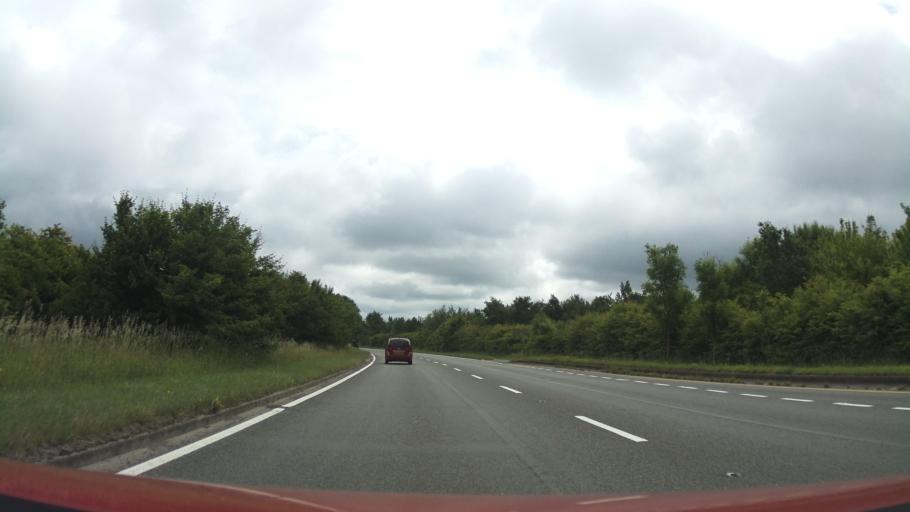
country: GB
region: England
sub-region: Leicestershire
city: Ashby de la Zouch
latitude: 52.7619
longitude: -1.4853
